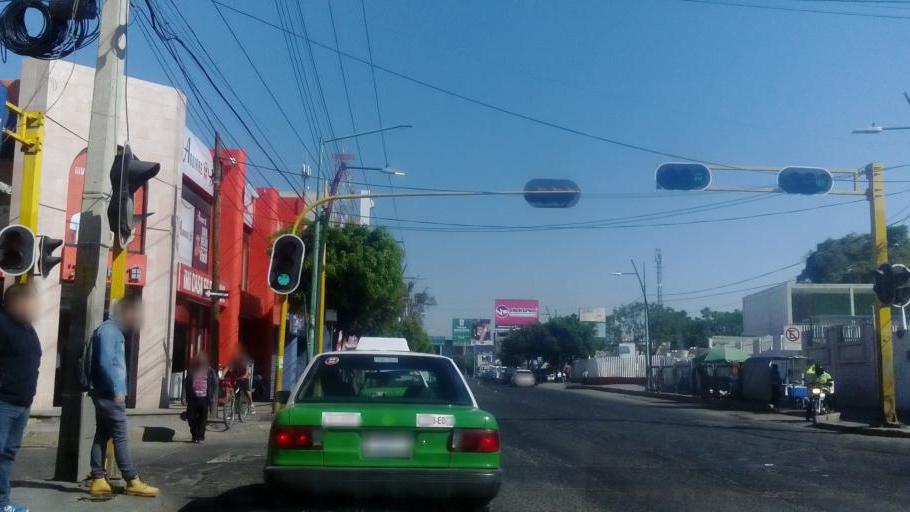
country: MX
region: Guanajuato
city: Leon
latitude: 21.1249
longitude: -101.6860
